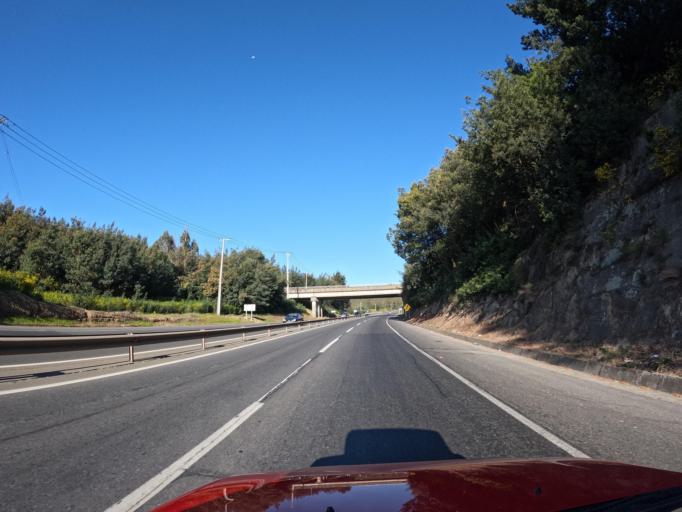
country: CL
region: Biobio
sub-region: Provincia de Concepcion
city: Penco
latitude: -36.7532
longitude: -72.9815
